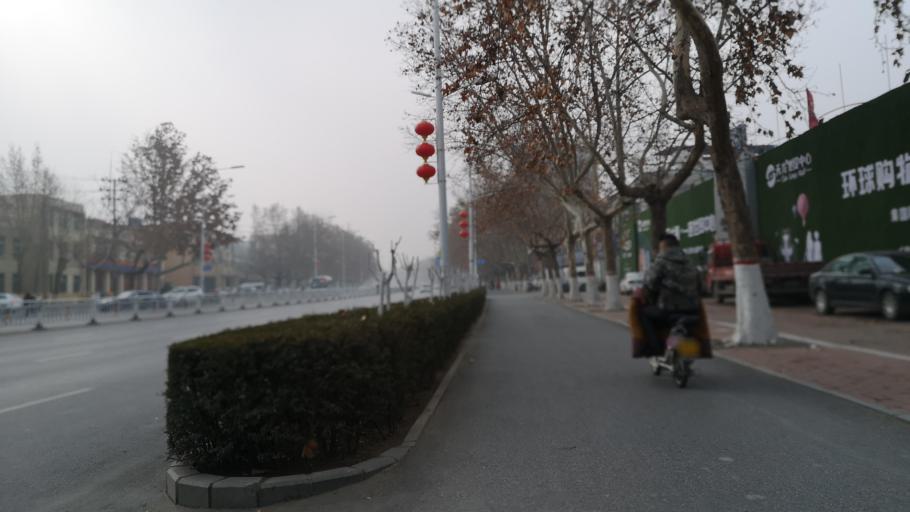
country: CN
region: Henan Sheng
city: Zhongyuanlu
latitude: 35.7757
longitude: 115.0408
